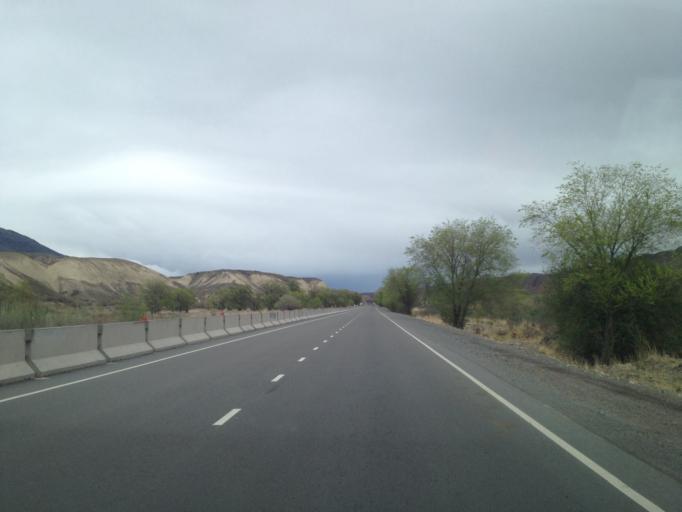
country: KG
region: Naryn
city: Kochkor
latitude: 42.4701
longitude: 75.8871
